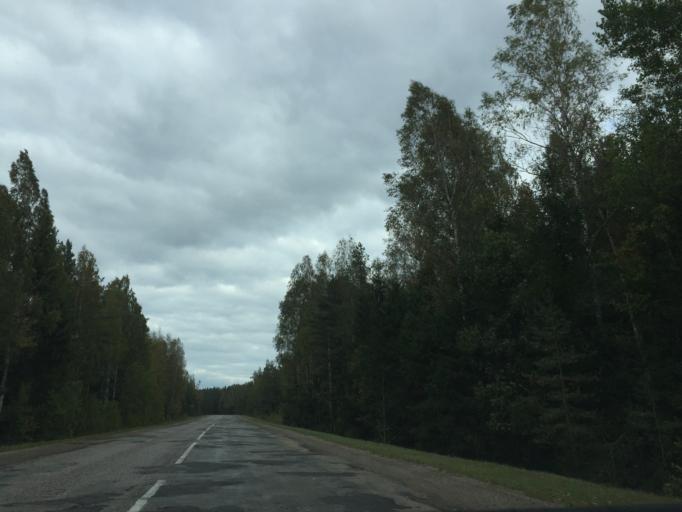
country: LV
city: Tireli
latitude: 56.8612
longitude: 23.5382
